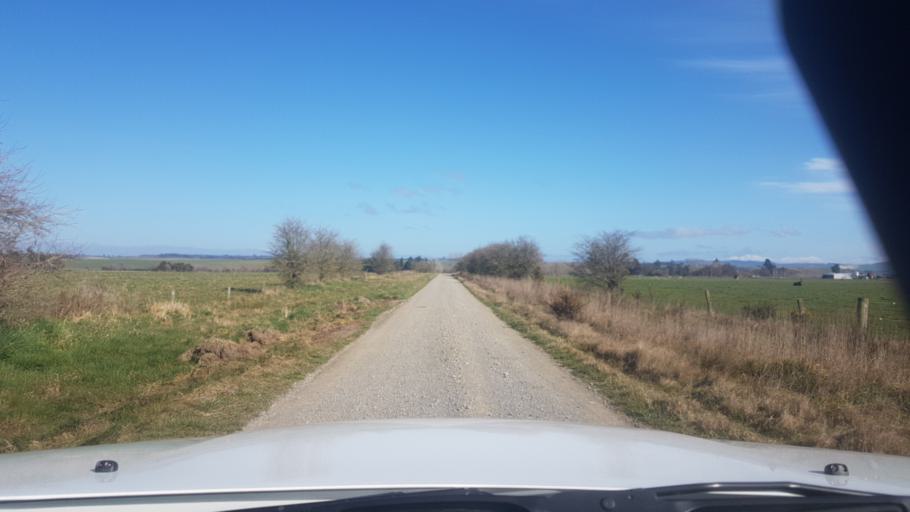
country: NZ
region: Canterbury
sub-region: Timaru District
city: Pleasant Point
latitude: -44.1718
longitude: 171.2286
